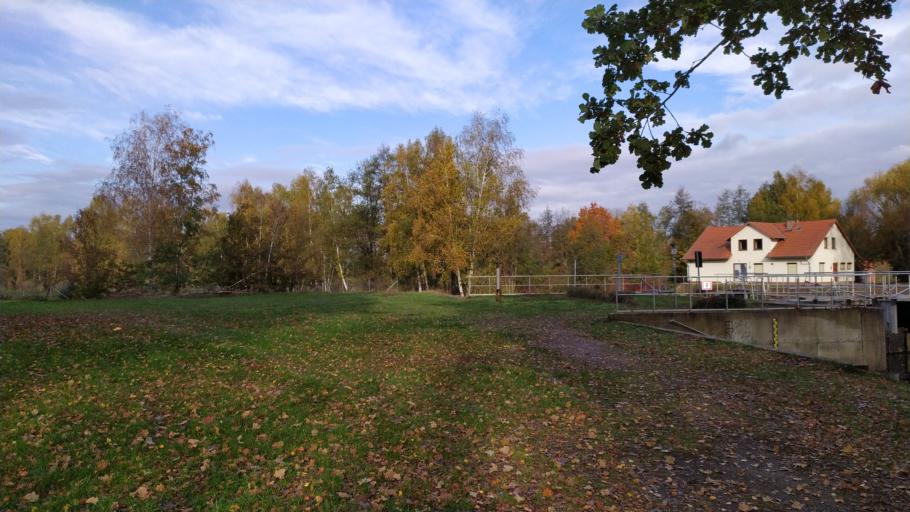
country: DE
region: Brandenburg
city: Schlepzig
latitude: 52.0844
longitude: 13.8768
